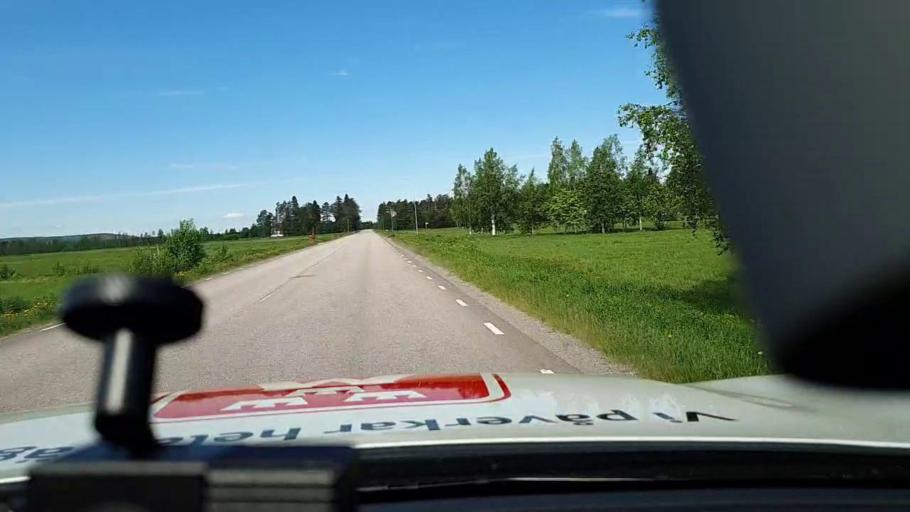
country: SE
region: Norrbotten
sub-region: Lulea Kommun
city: Sodra Sunderbyn
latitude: 65.6390
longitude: 21.9065
